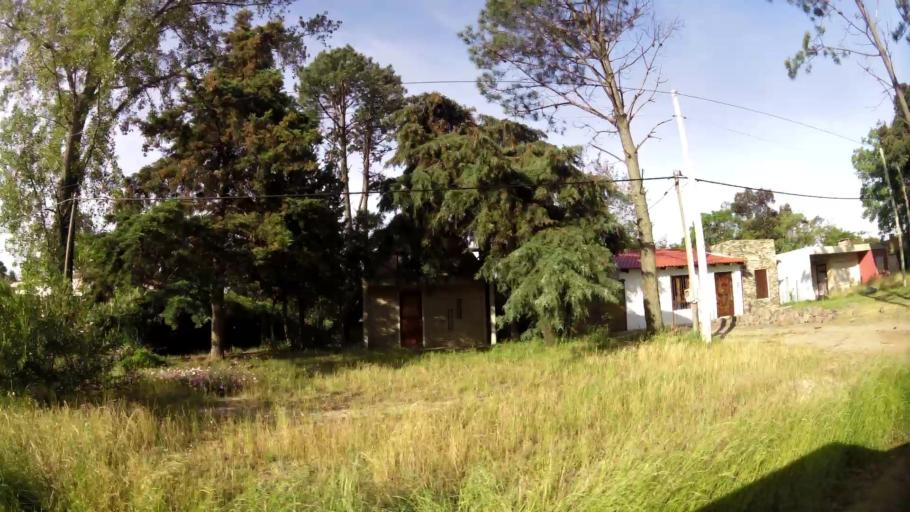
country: UY
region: Canelones
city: Empalme Olmos
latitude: -34.7853
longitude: -55.8576
